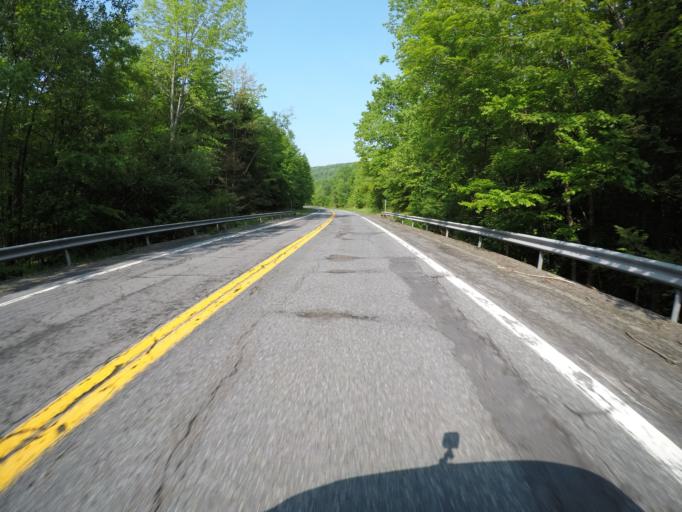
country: US
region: New York
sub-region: Sullivan County
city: Livingston Manor
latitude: 42.1031
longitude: -74.7903
